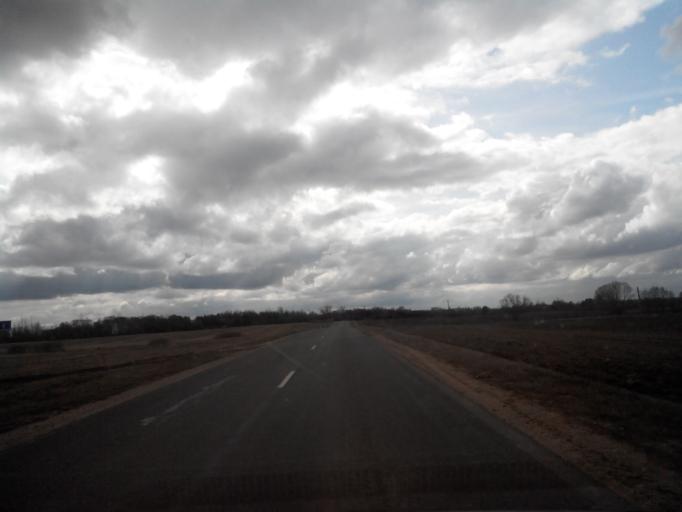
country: BY
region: Vitebsk
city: Pastavy
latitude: 55.1374
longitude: 26.9473
